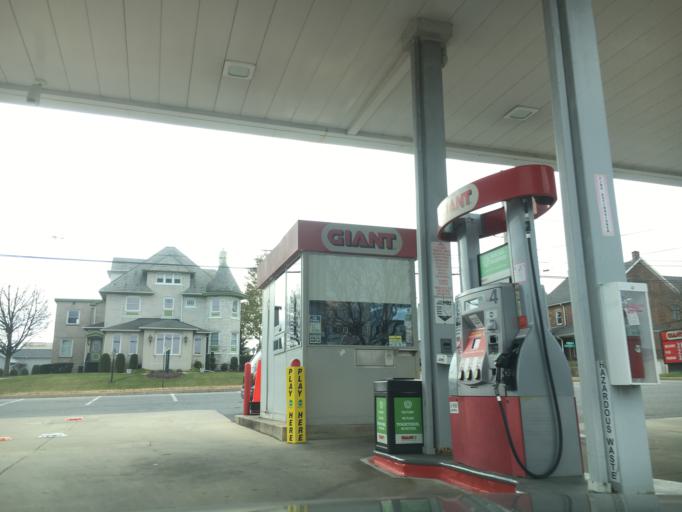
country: US
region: Pennsylvania
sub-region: Lehigh County
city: Coplay
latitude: 40.6733
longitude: -75.4951
